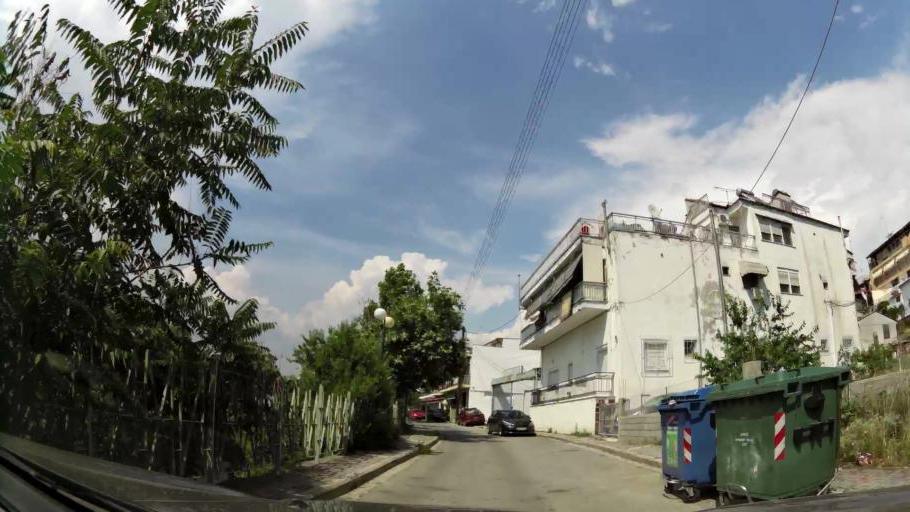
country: GR
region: Central Macedonia
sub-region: Nomos Thessalonikis
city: Stavroupoli
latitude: 40.6737
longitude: 22.9401
